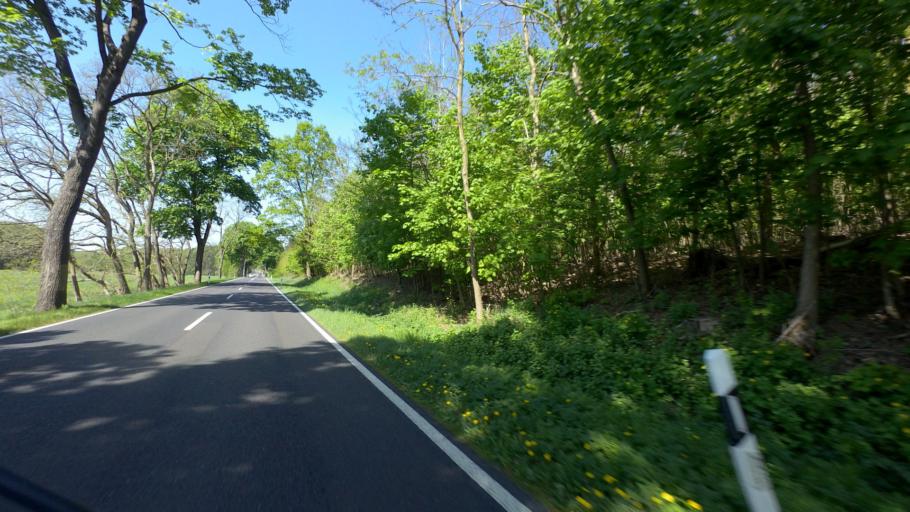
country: DE
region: Brandenburg
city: Friedland
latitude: 52.0608
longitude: 14.2787
